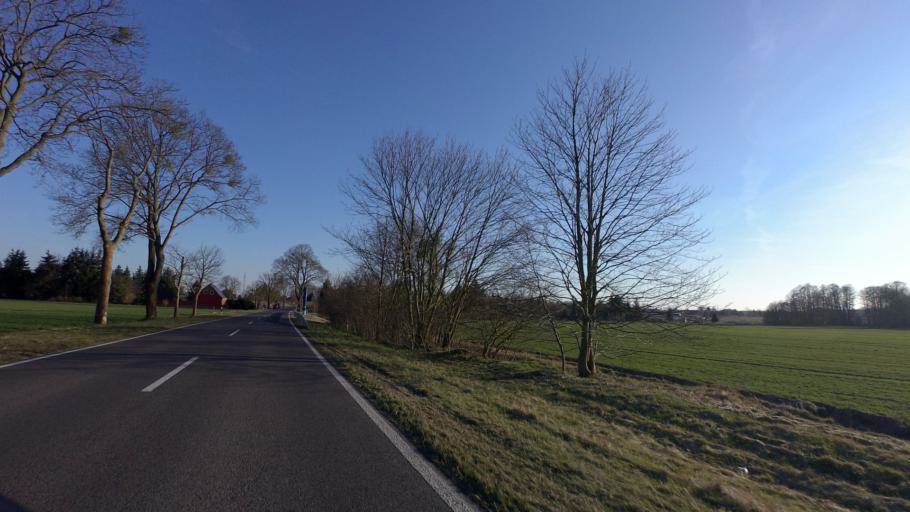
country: DE
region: Brandenburg
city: Eberswalde
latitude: 52.7863
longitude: 13.8389
